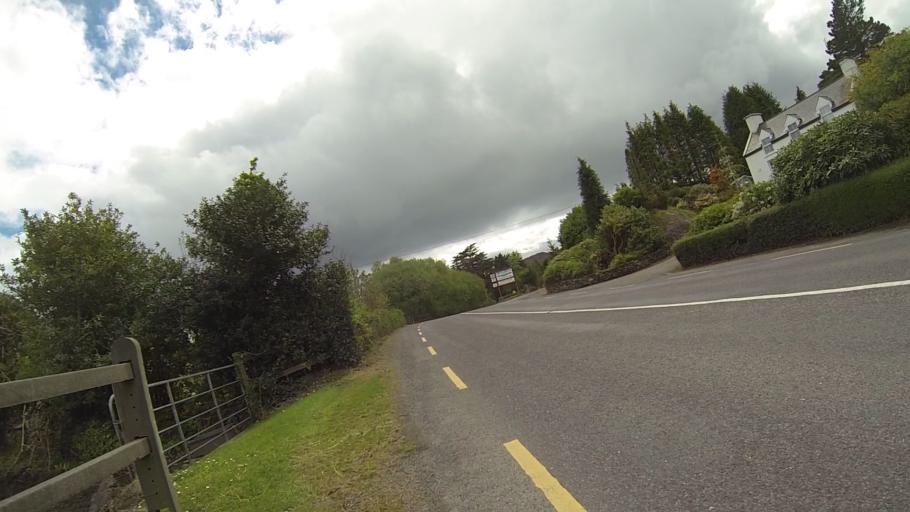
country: IE
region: Munster
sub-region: County Cork
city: Bantry
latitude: 51.7370
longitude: -9.5591
